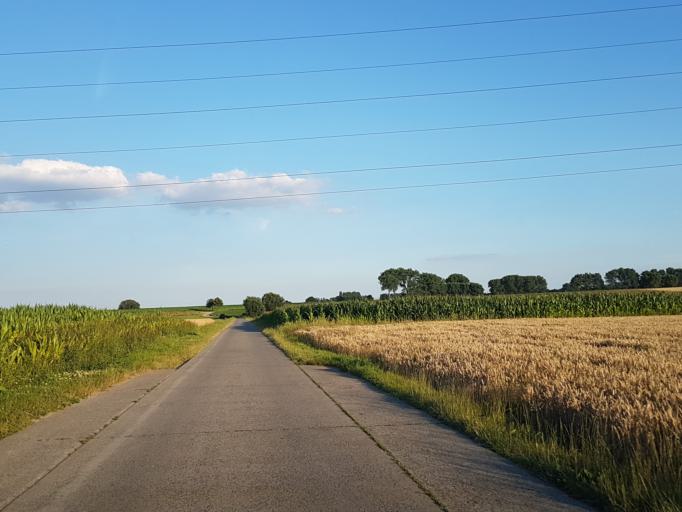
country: BE
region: Flanders
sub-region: Provincie Vlaams-Brabant
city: Wemmel
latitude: 50.9049
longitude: 4.2613
